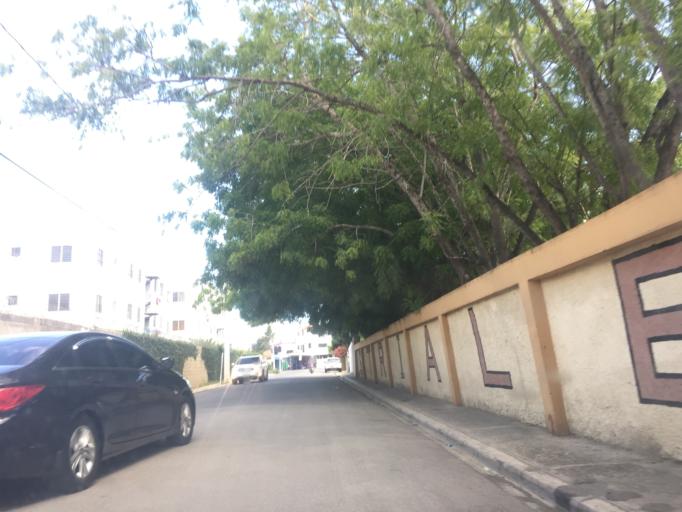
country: DO
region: Santiago
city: Santiago de los Caballeros
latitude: 19.4359
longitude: -70.6776
